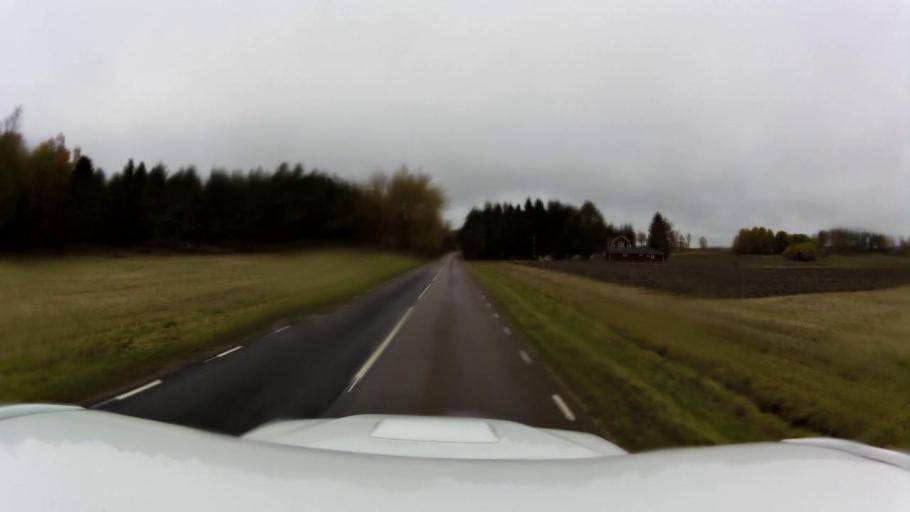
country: SE
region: OEstergoetland
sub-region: Norrkopings Kommun
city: Kimstad
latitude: 58.4177
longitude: 15.9160
